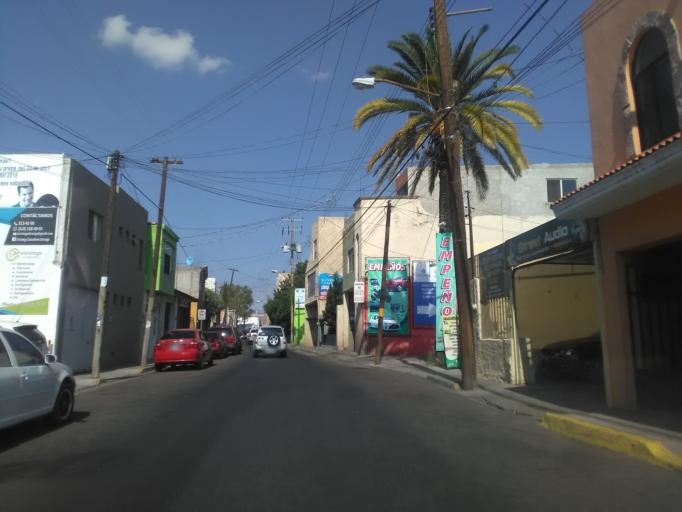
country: MX
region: Durango
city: Victoria de Durango
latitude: 24.0287
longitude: -104.6598
